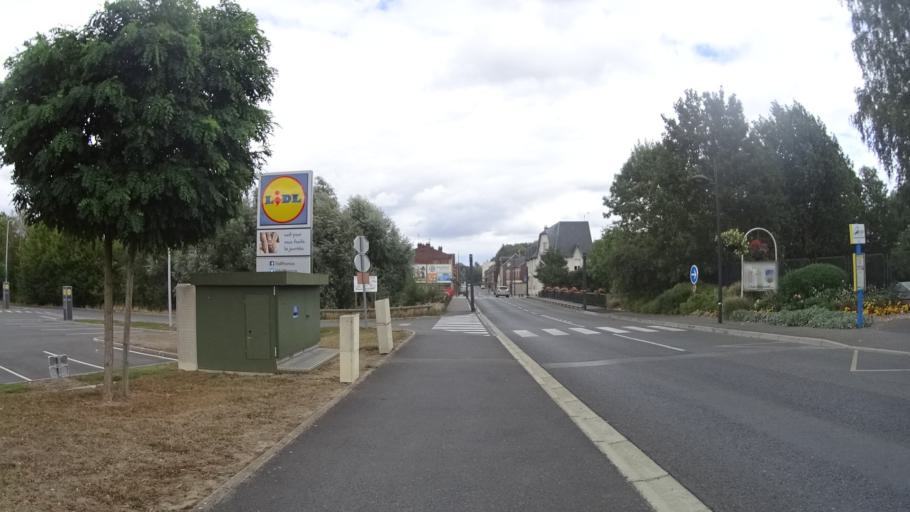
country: FR
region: Picardie
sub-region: Departement de l'Aisne
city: Beautor
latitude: 49.6618
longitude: 3.3517
